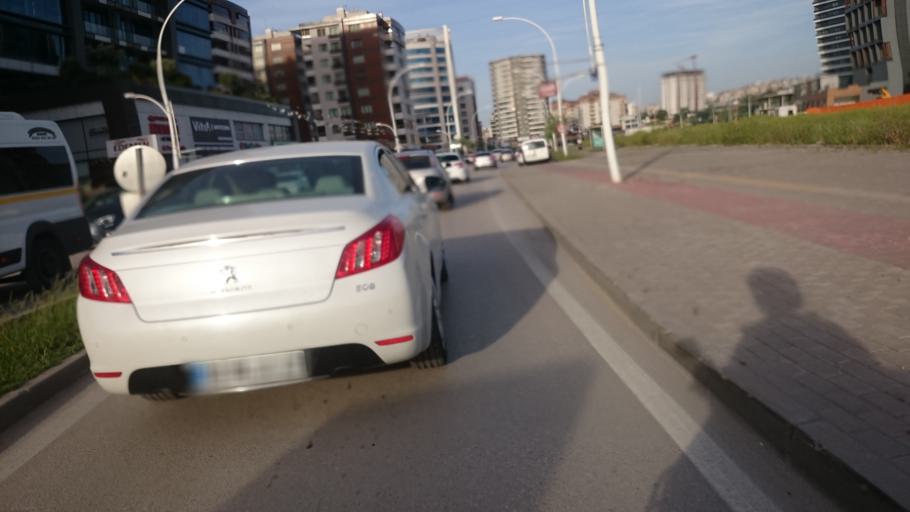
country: TR
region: Bursa
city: Cali
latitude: 40.2164
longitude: 28.9382
